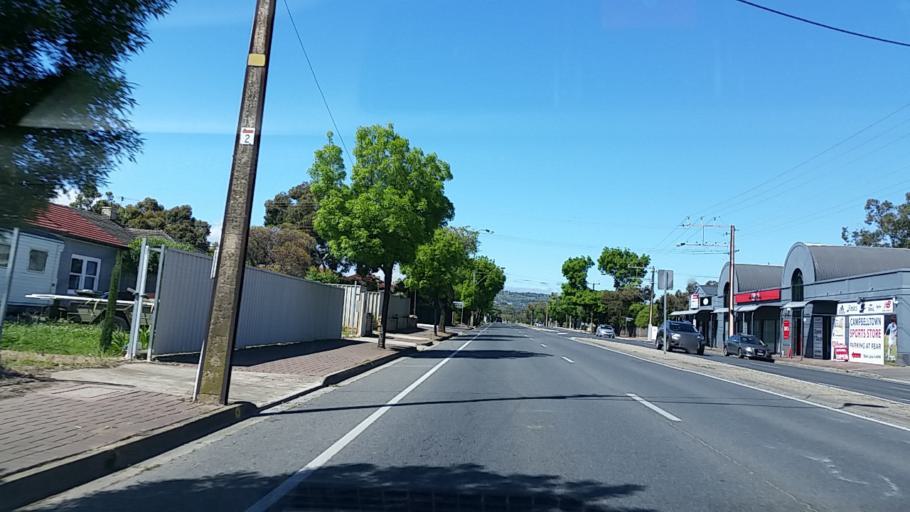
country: AU
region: South Australia
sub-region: Campbelltown
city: Hectorville
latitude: -34.9074
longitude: 138.6579
